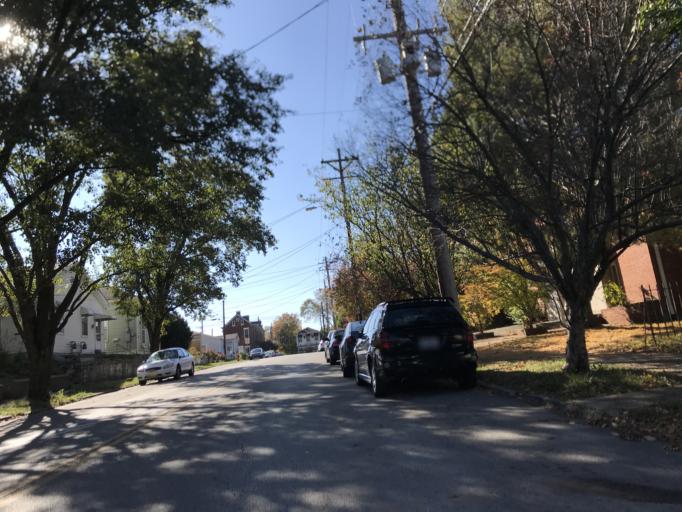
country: US
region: Indiana
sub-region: Clark County
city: Jeffersonville
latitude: 38.2469
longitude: -85.7277
